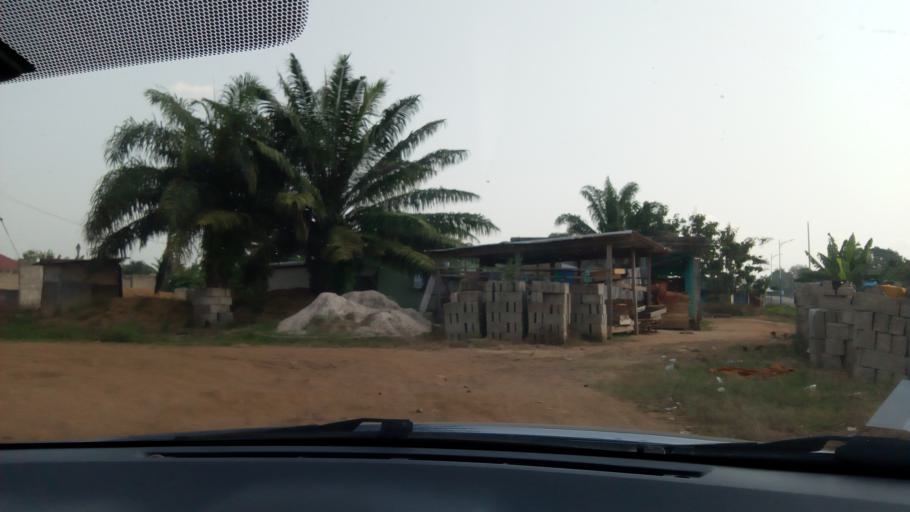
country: GH
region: Western
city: Bibiani
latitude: 6.7911
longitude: -2.5166
